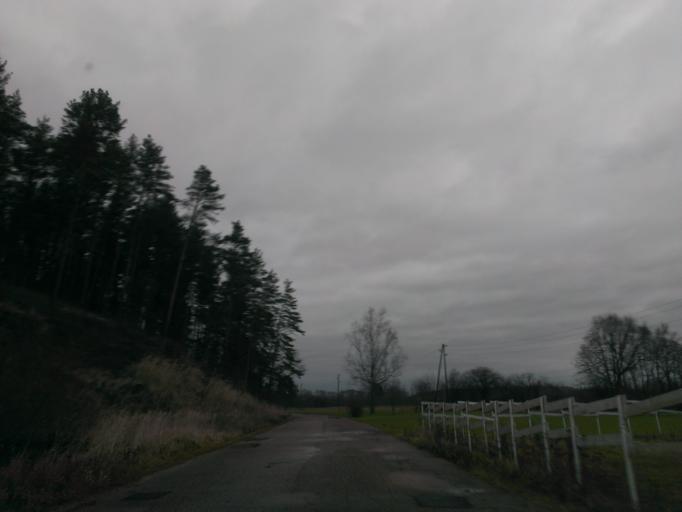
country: LV
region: Adazi
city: Adazi
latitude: 57.0621
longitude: 24.3565
